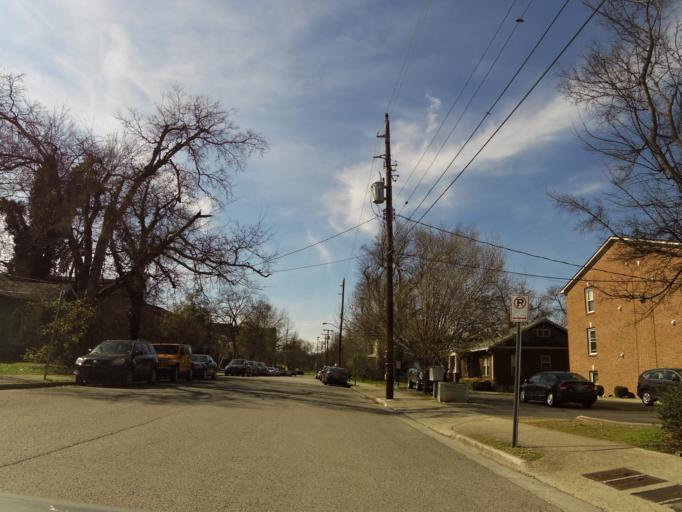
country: US
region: Tennessee
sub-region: Davidson County
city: Nashville
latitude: 36.1359
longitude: -86.8032
